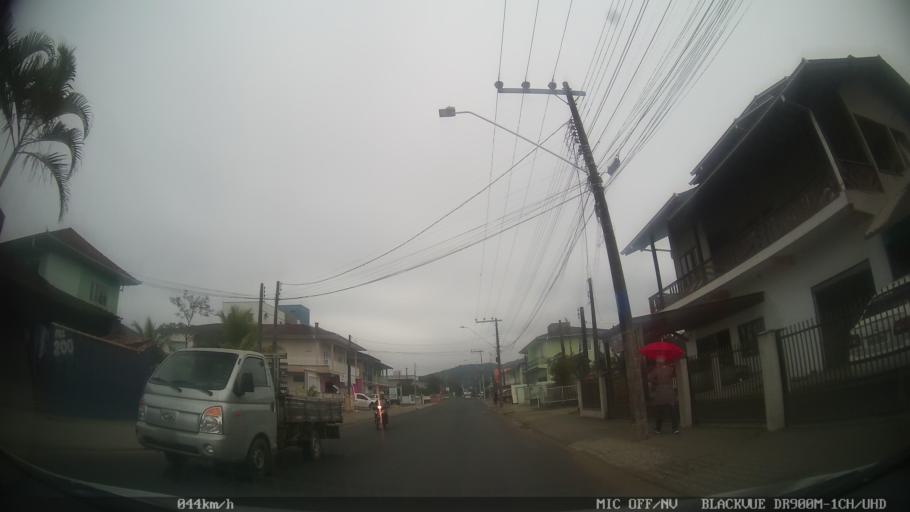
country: BR
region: Santa Catarina
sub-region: Joinville
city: Joinville
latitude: -26.2420
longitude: -48.8108
